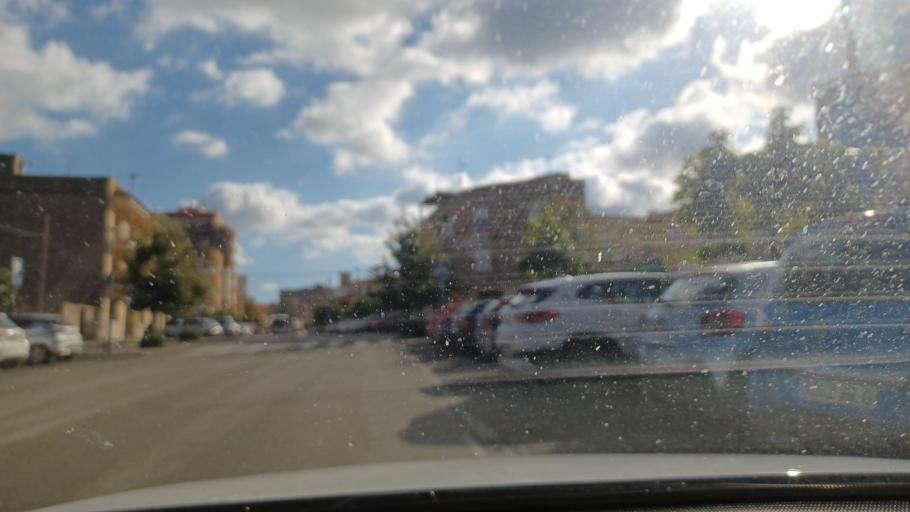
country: ES
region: Valencia
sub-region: Provincia de Castello
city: Betxi
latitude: 39.9307
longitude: -0.1969
